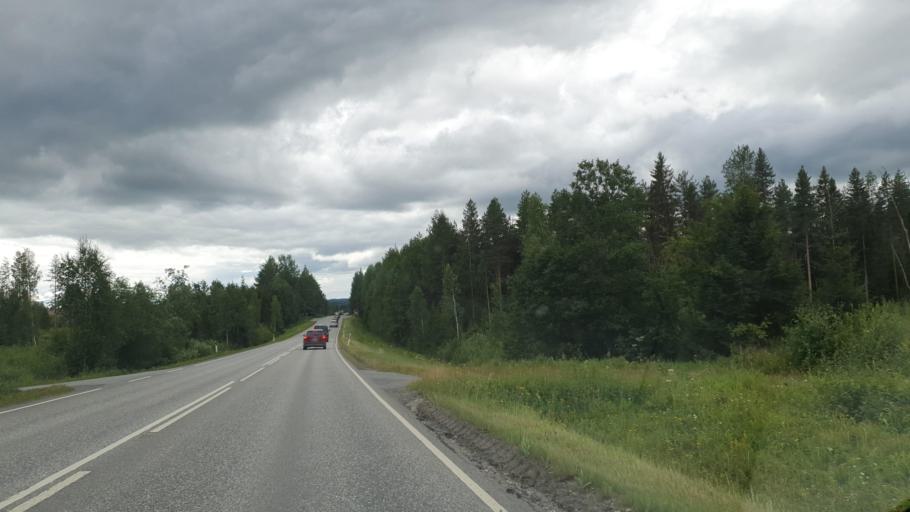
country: FI
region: Northern Savo
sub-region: Ylae-Savo
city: Sonkajaervi
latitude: 63.7425
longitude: 27.3819
